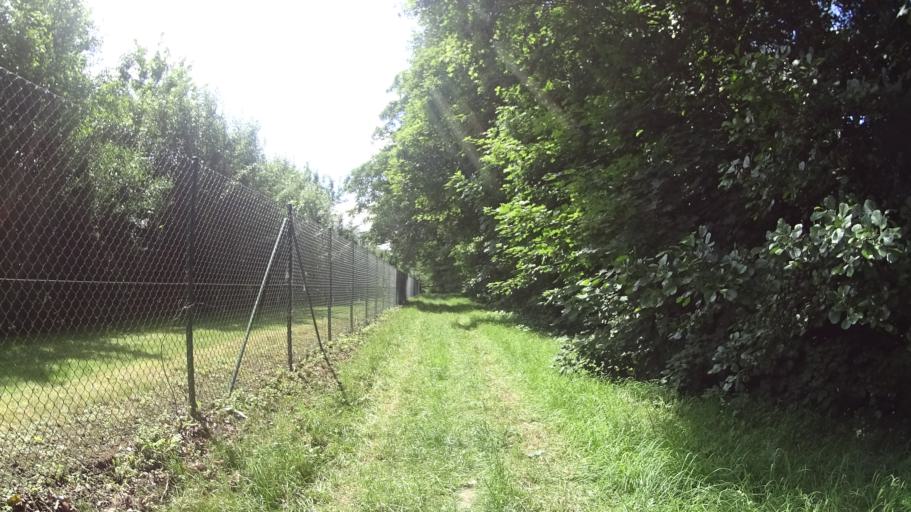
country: DE
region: Lower Saxony
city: Algermissen
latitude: 52.2499
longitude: 9.9522
